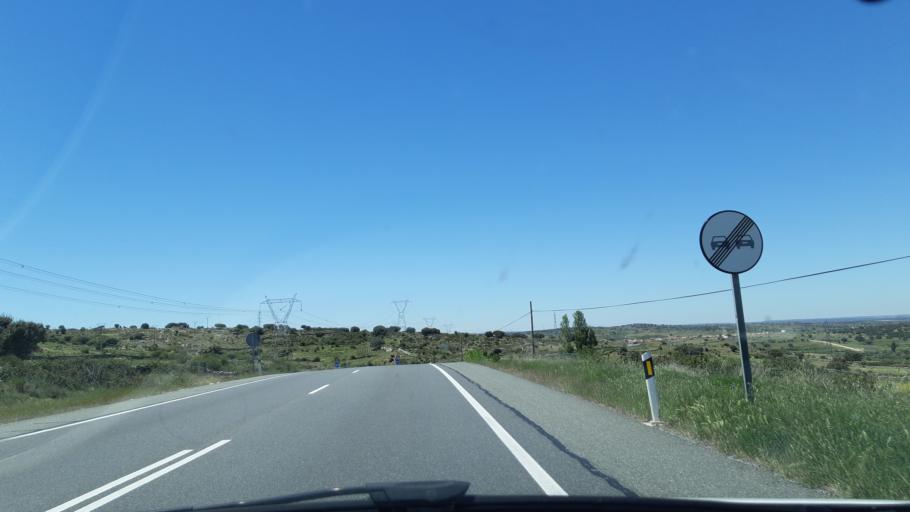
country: ES
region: Castille and Leon
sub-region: Provincia de Segovia
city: Vegas de Matute
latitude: 40.7490
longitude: -4.3027
